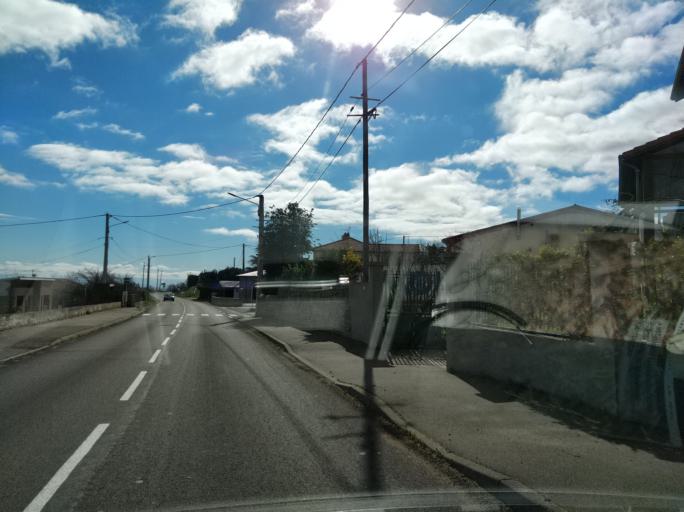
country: FR
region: Rhone-Alpes
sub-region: Departement de la Loire
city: Pelussin
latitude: 45.4029
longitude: 4.6839
